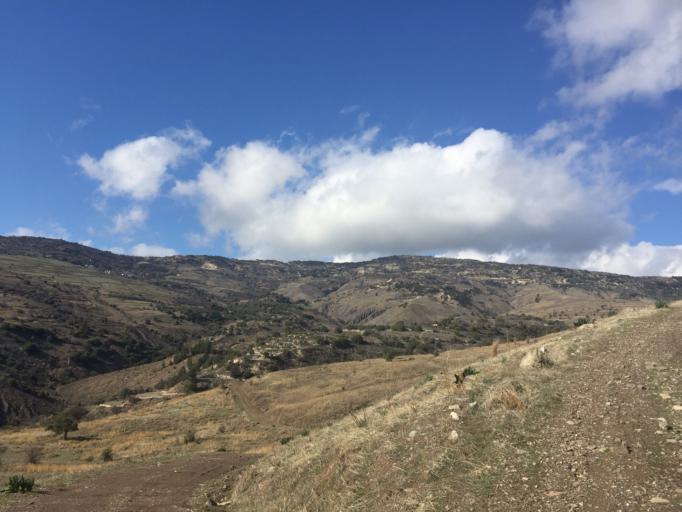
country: CY
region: Limassol
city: Pachna
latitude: 34.8753
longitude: 32.6545
